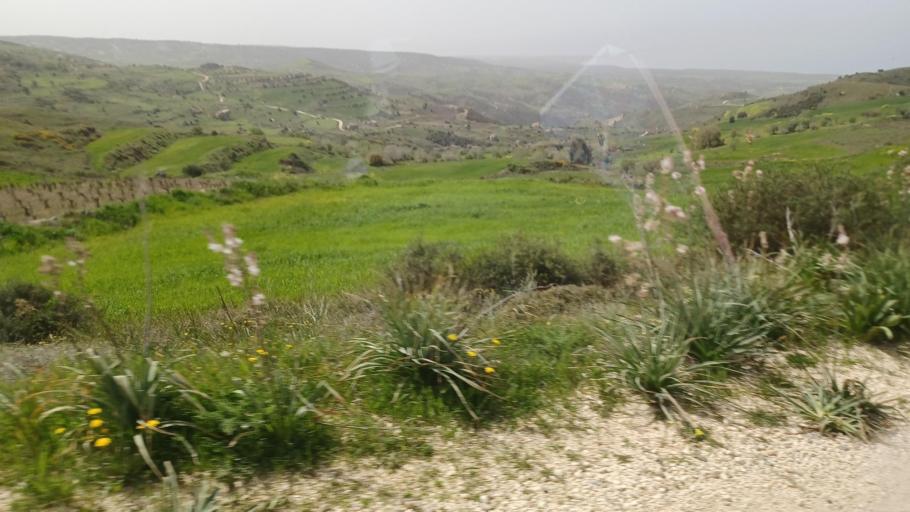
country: CY
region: Pafos
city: Polis
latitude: 34.9757
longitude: 32.3621
